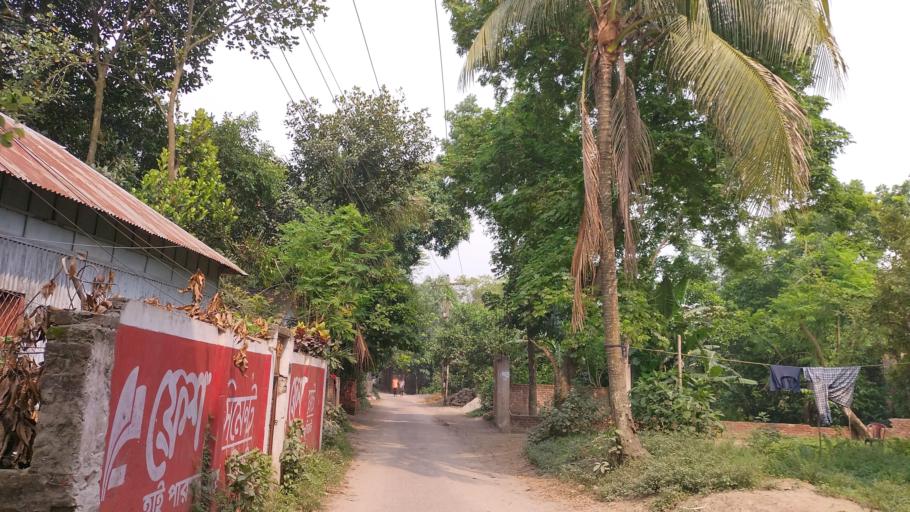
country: BD
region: Dhaka
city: Azimpur
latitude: 23.6895
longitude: 90.3025
